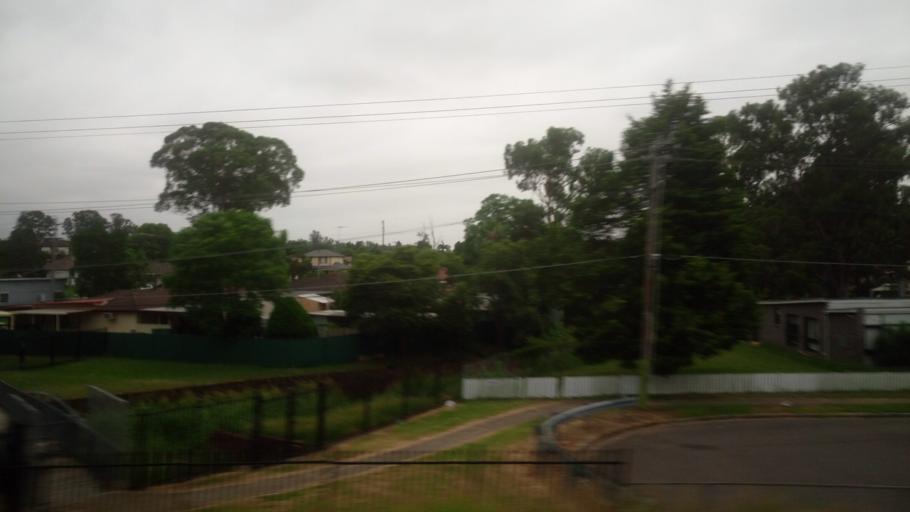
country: AU
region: New South Wales
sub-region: Penrith Municipality
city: Werrington County
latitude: -33.7587
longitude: 150.7318
